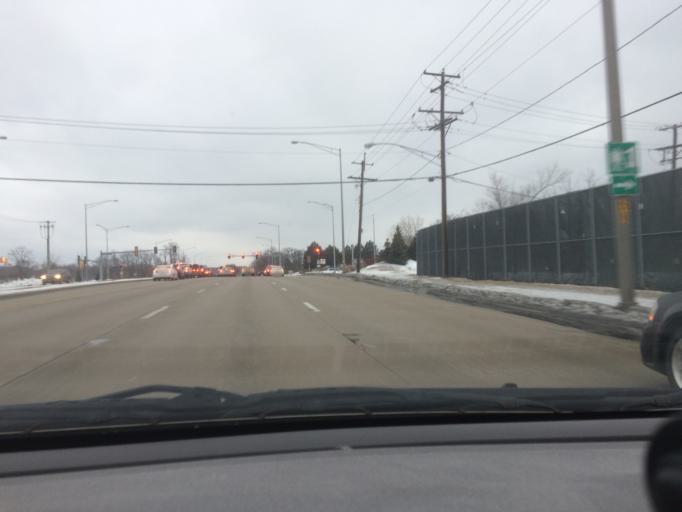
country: US
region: Illinois
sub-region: DuPage County
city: Bloomingdale
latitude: 41.9543
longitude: -88.0493
